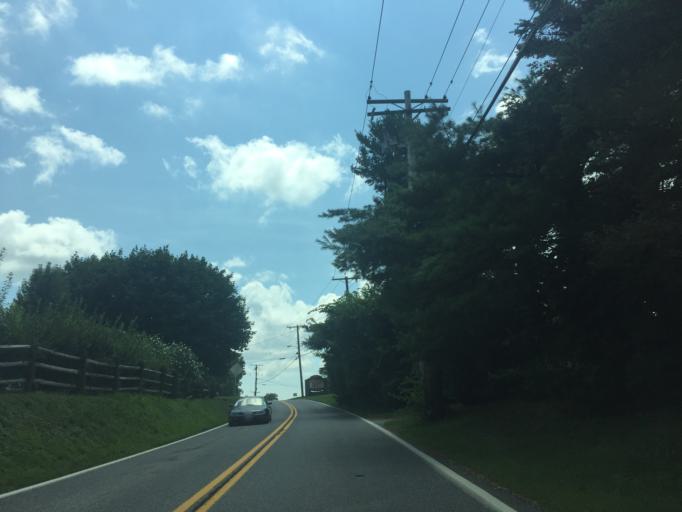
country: US
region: Maryland
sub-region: Baltimore County
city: Kingsville
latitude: 39.4440
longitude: -76.4151
